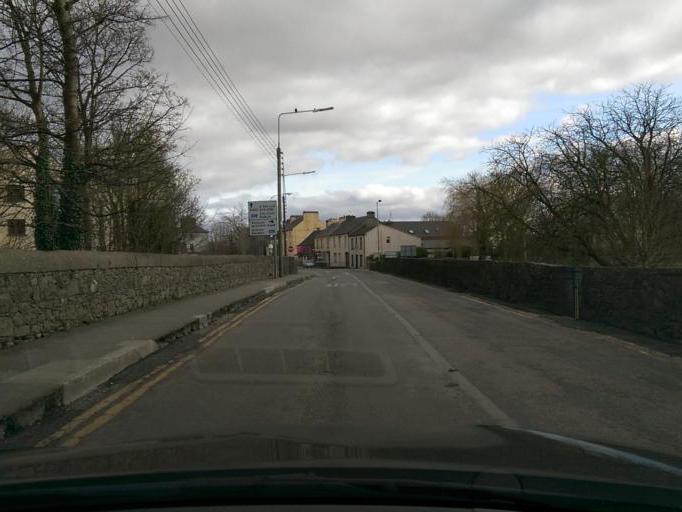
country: IE
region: Connaught
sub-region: County Galway
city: Ballinasloe
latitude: 53.3309
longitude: -8.2184
